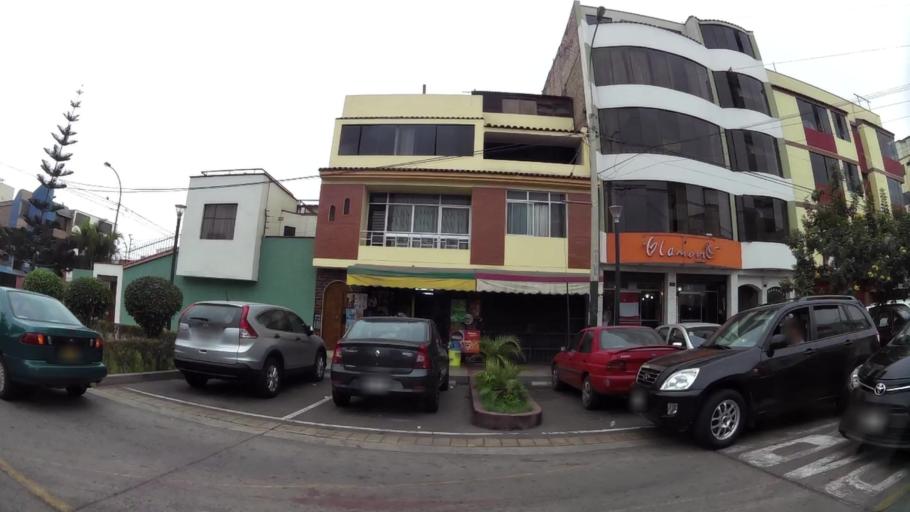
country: PE
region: Lima
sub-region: Lima
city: Surco
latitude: -12.1392
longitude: -76.9885
